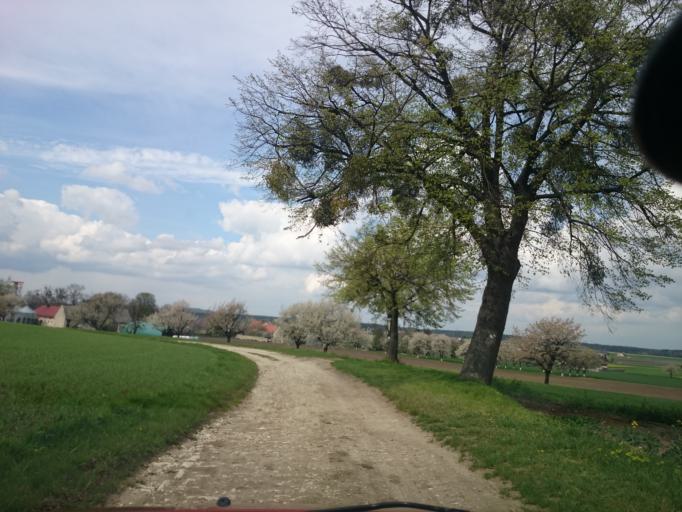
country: PL
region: Opole Voivodeship
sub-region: Powiat krapkowicki
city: Rozwadza
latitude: 50.4892
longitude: 18.1247
